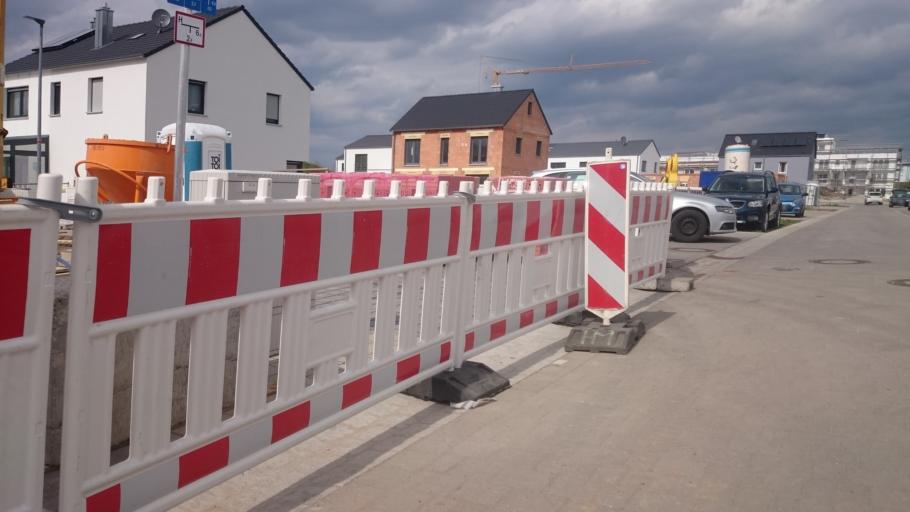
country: DE
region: Bavaria
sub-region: Regierungsbezirk Mittelfranken
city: Hilpoltstein
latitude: 49.1925
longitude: 11.1783
